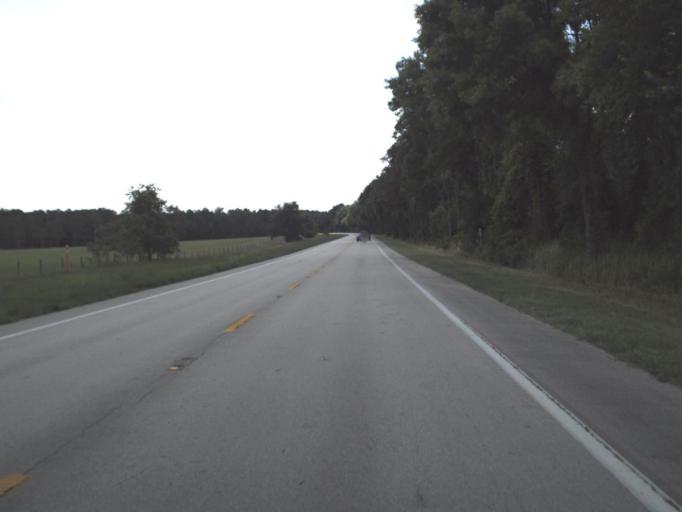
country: US
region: Florida
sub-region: Putnam County
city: Palatka
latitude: 29.5325
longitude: -81.6429
